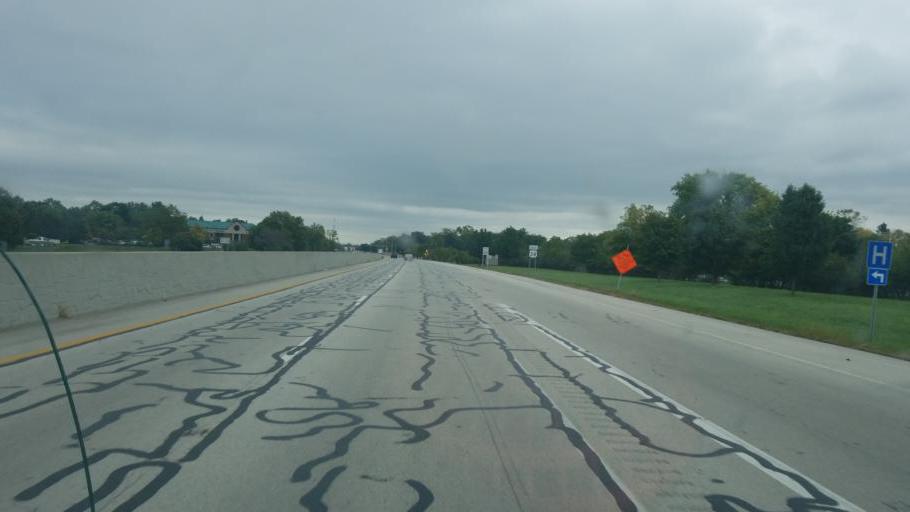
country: US
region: Ohio
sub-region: Lucas County
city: Maumee
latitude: 41.5558
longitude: -83.6800
